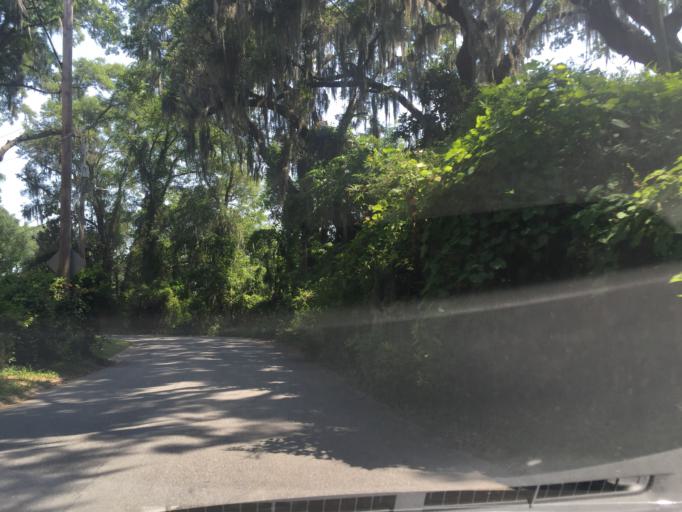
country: US
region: Georgia
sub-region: Chatham County
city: Montgomery
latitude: 31.9676
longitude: -81.1256
